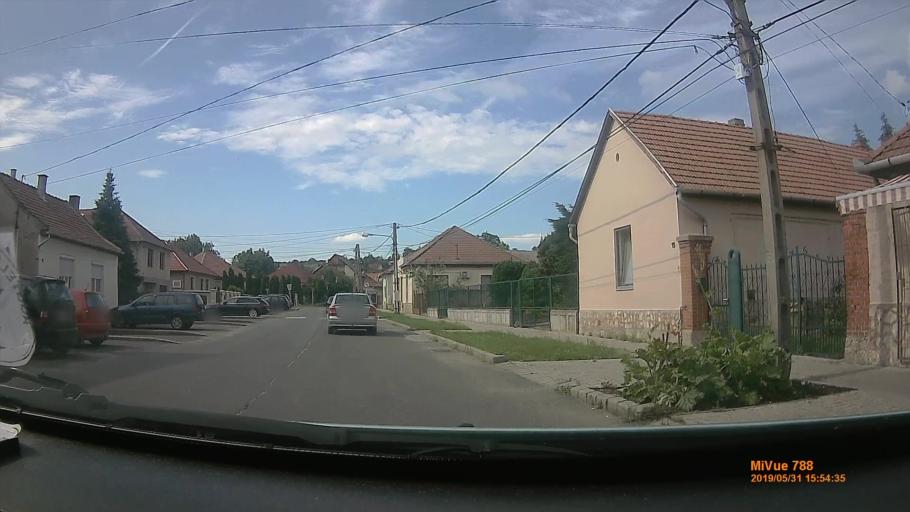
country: HU
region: Borsod-Abauj-Zemplen
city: Szerencs
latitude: 48.1610
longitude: 21.2005
